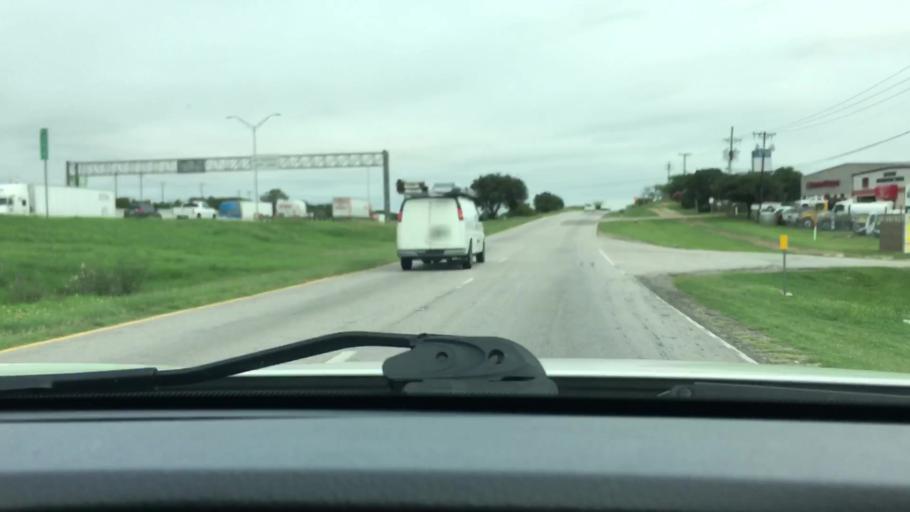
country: US
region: Texas
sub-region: Williamson County
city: Round Rock
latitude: 30.5443
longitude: -97.6919
